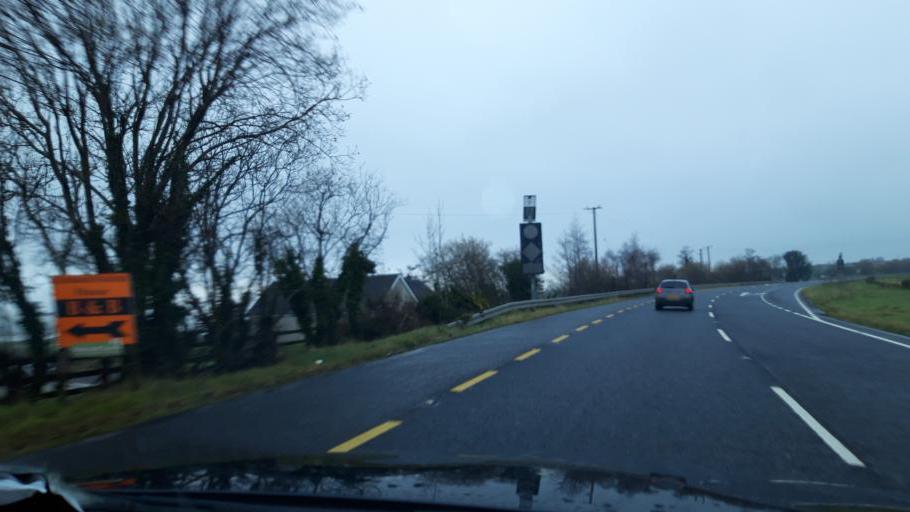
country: IE
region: Ulster
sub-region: County Donegal
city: Letterkenny
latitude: 54.9510
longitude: -7.6658
